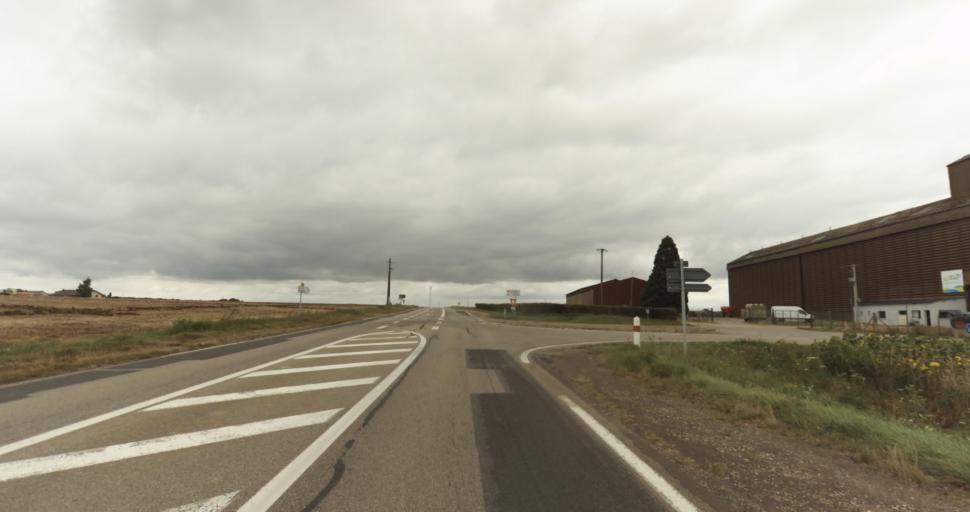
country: FR
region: Haute-Normandie
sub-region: Departement de l'Eure
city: Gravigny
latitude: 49.0716
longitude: 1.2214
